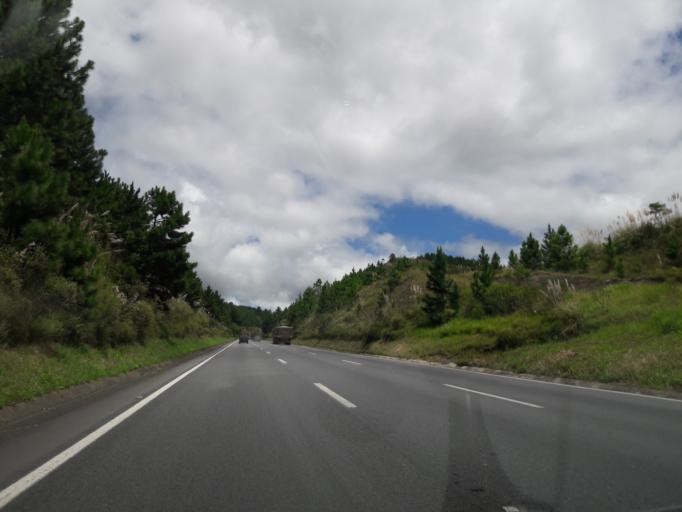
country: BR
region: Parana
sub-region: Campina Grande Do Sul
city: Campina Grande do Sul
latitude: -25.1026
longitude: -48.8336
